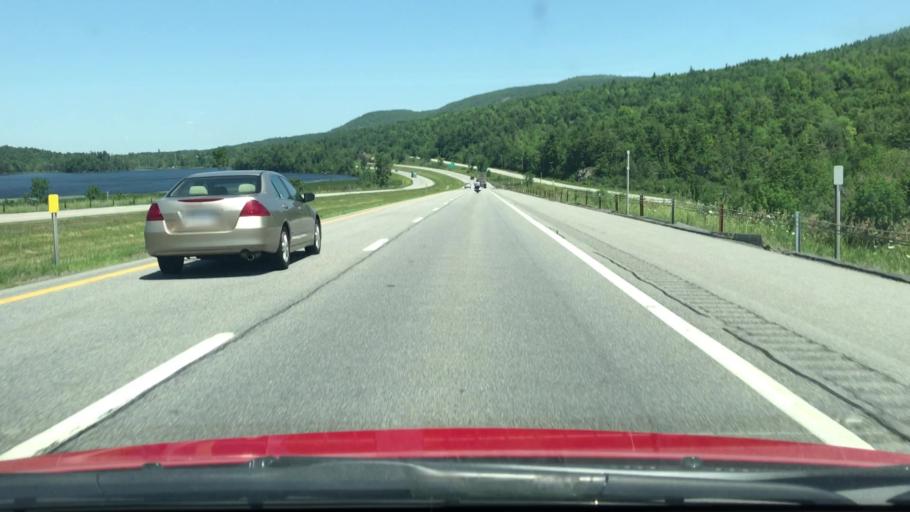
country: US
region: New York
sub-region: Essex County
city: Keeseville
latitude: 44.4192
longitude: -73.4961
